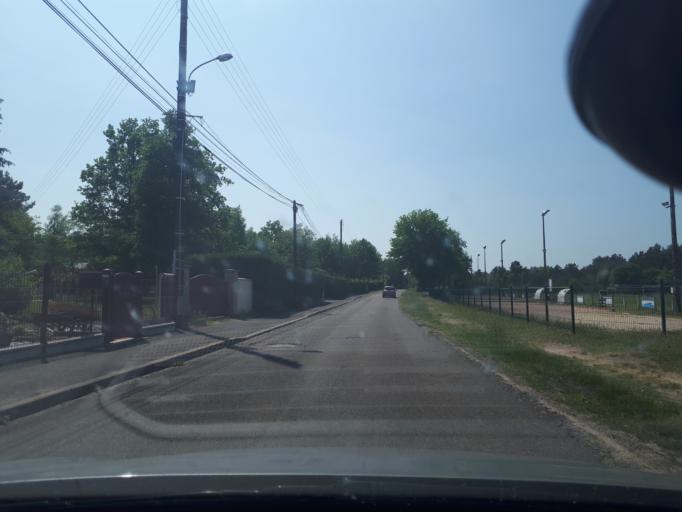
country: FR
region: Pays de la Loire
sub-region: Departement de la Sarthe
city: Le Breil-sur-Merize
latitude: 48.0014
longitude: 0.4783
